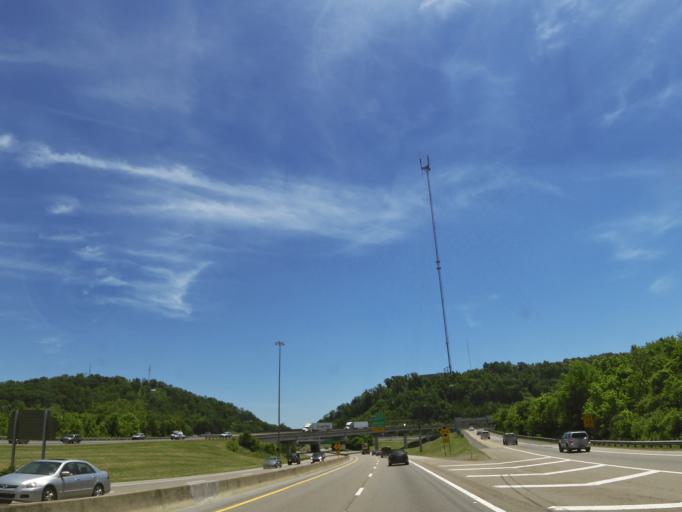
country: US
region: Tennessee
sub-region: Knox County
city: Knoxville
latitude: 36.0026
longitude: -83.9615
